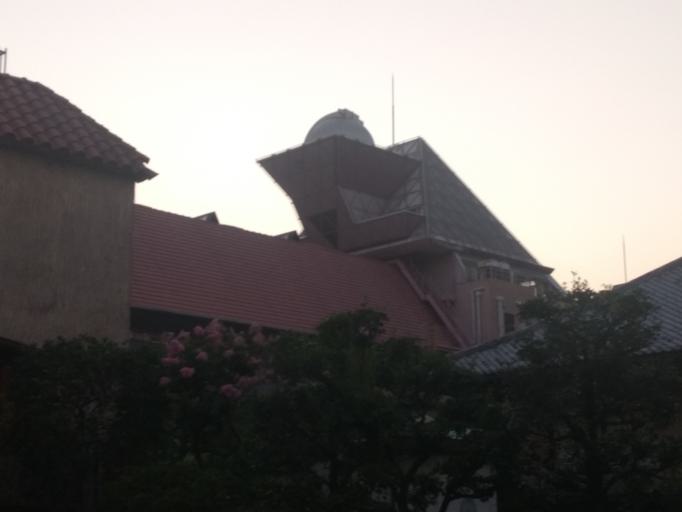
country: JP
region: Tokyo
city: Tokyo
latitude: 35.7035
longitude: 139.7578
